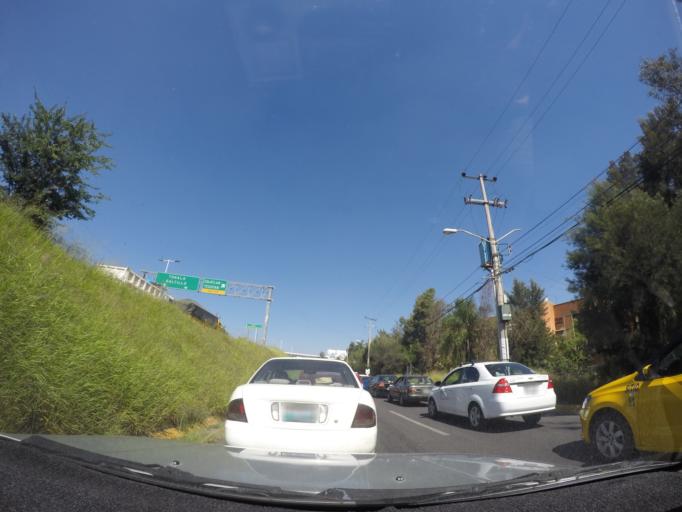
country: MX
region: Jalisco
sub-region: Tonala
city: Mismaloya (Fraccionamiento Pedregal de Santa Martha)
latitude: 20.6058
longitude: -103.1386
